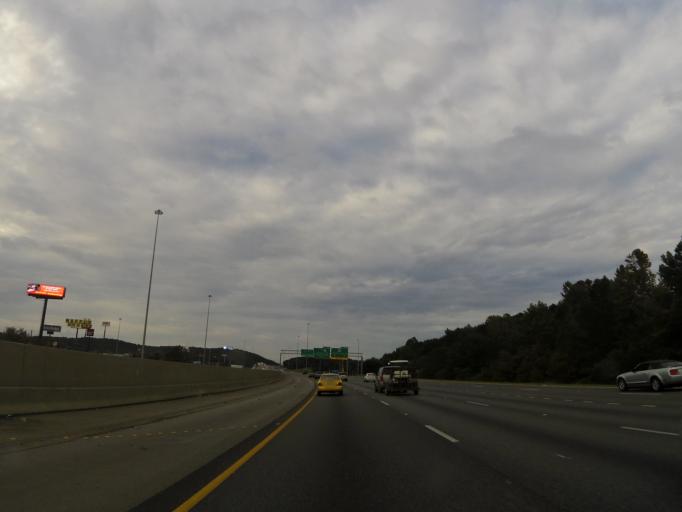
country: US
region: Alabama
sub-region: Shelby County
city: Indian Springs Village
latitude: 33.3318
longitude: -86.7794
